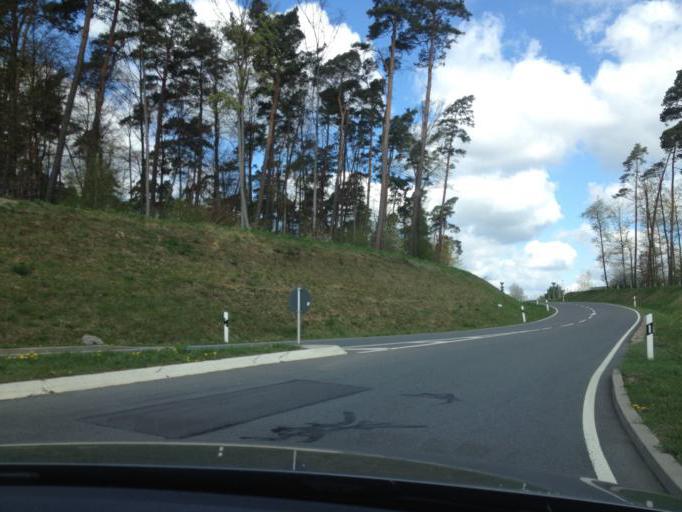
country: DE
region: Baden-Wuerttemberg
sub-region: Karlsruhe Region
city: Osterburken
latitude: 49.4163
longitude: 9.4489
